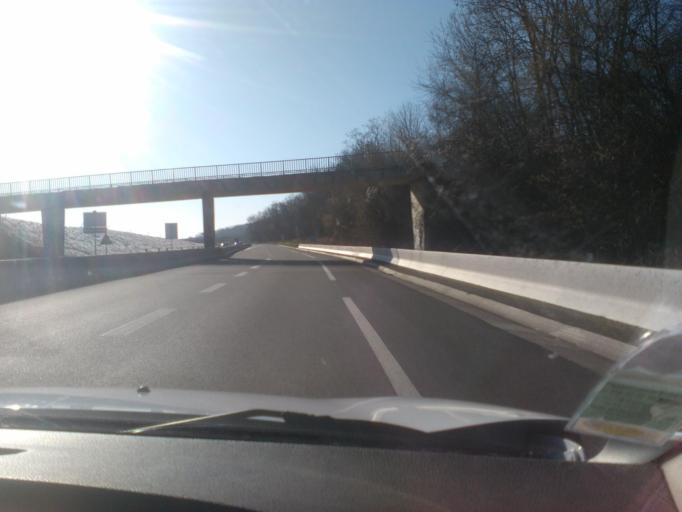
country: FR
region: Alsace
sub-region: Departement du Bas-Rhin
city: Mutzig
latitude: 48.5244
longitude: 7.4661
